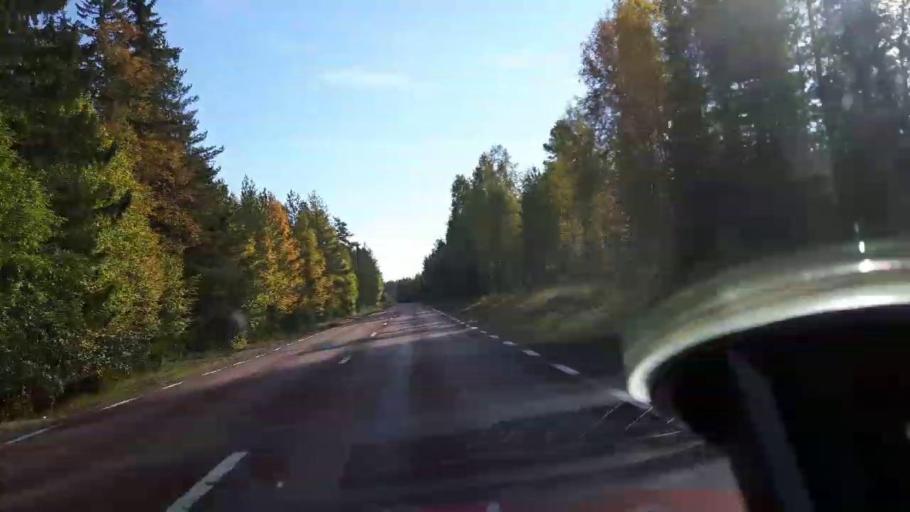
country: SE
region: Gaevleborg
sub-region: Ljusdals Kommun
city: Farila
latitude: 61.9272
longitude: 15.5699
